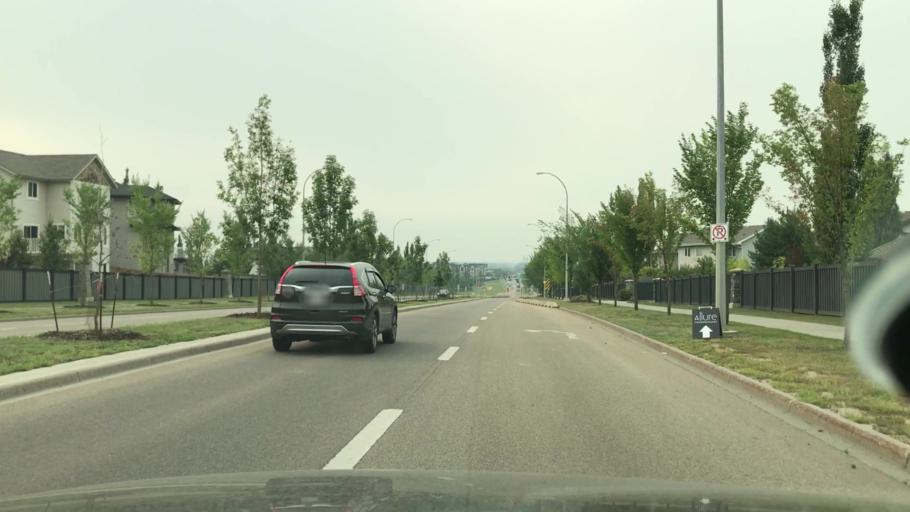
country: CA
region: Alberta
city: Edmonton
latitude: 53.4477
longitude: -113.5657
